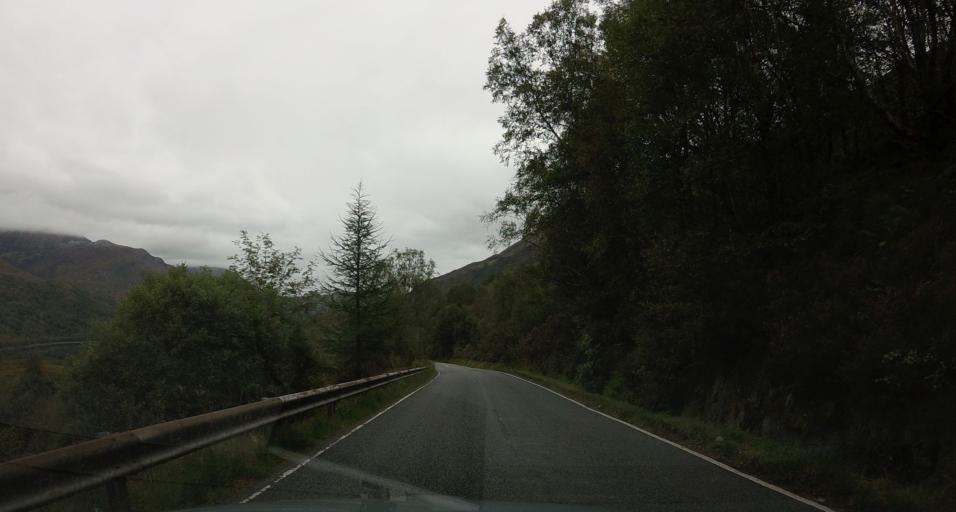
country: GB
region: Scotland
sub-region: Highland
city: Fort William
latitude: 56.7037
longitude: -5.0307
